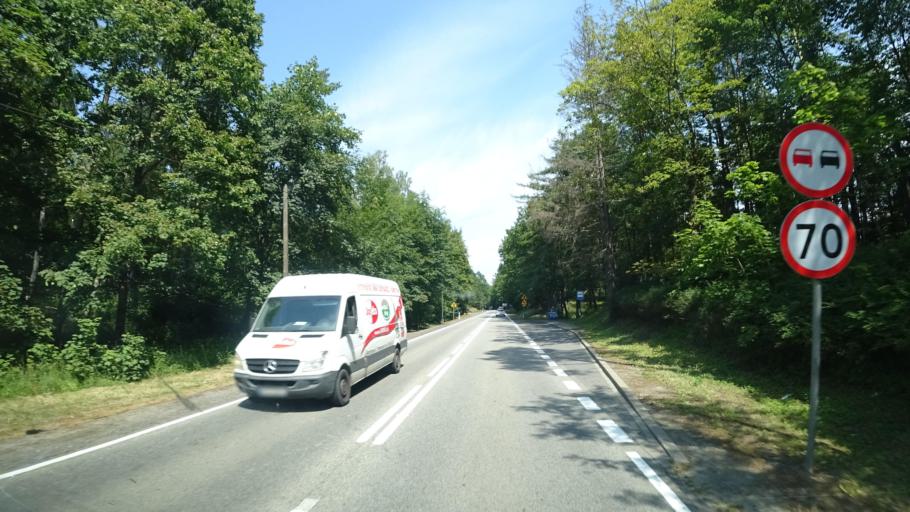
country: PL
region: Pomeranian Voivodeship
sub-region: Powiat koscierski
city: Grabowo Koscierskie
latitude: 54.2146
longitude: 18.1178
